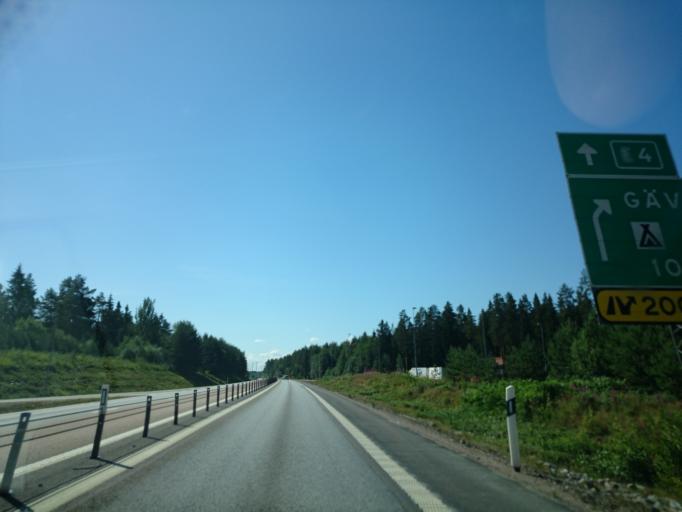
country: SE
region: Gaevleborg
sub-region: Gavle Kommun
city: Gavle
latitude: 60.6915
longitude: 17.0845
